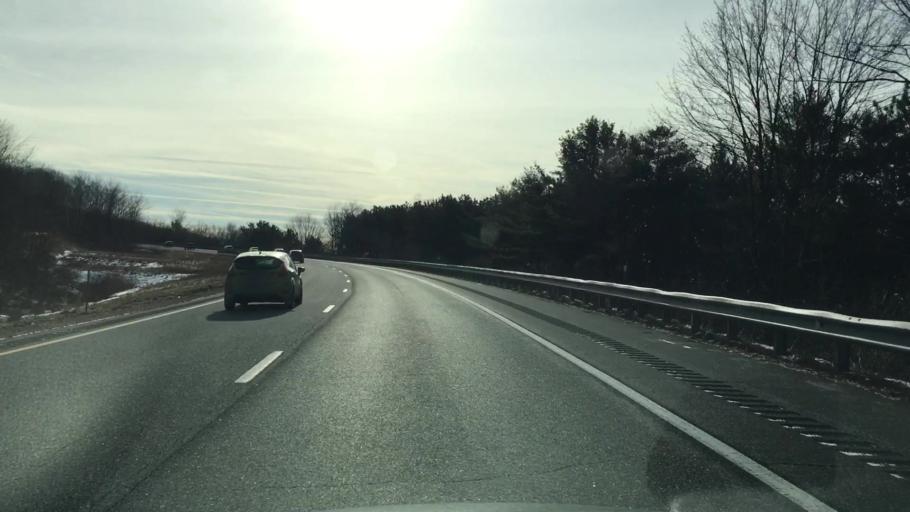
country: US
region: New Hampshire
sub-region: Sullivan County
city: Grantham
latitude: 43.4707
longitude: -72.1031
